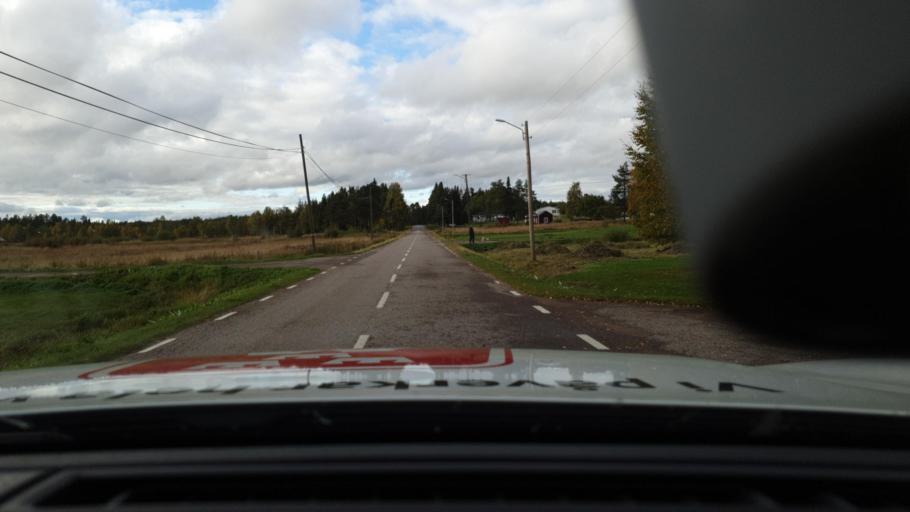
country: SE
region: Norrbotten
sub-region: Overkalix Kommun
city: OEverkalix
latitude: 67.0045
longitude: 22.4918
